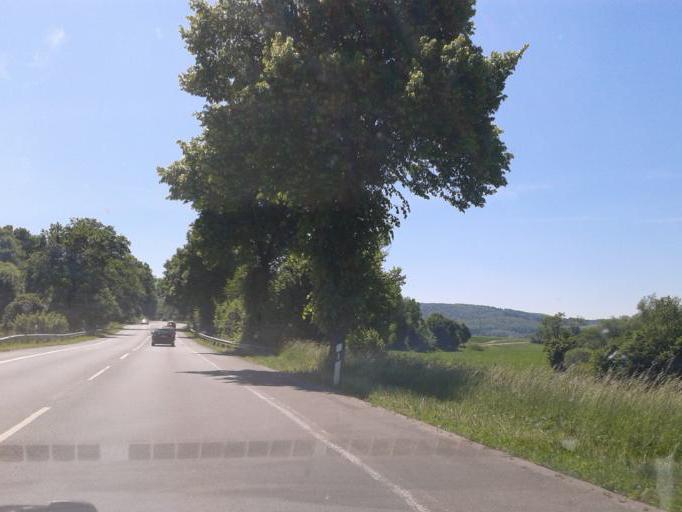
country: DE
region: North Rhine-Westphalia
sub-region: Regierungsbezirk Detmold
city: Lugde
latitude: 51.9384
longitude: 9.2358
